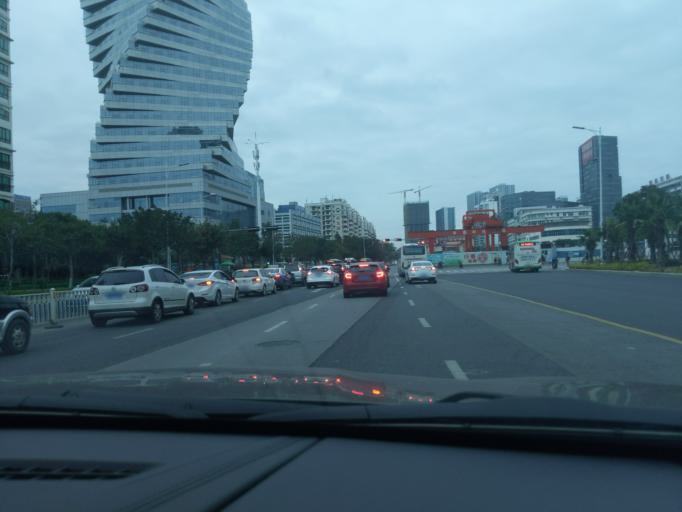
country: CN
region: Fujian
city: Liuwudian
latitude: 24.4846
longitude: 118.1762
